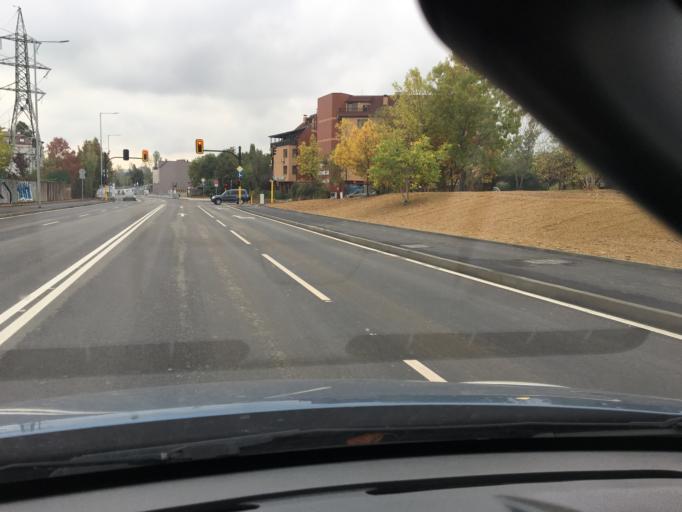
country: BG
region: Sofia-Capital
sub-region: Stolichna Obshtina
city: Sofia
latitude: 42.6848
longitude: 23.2681
